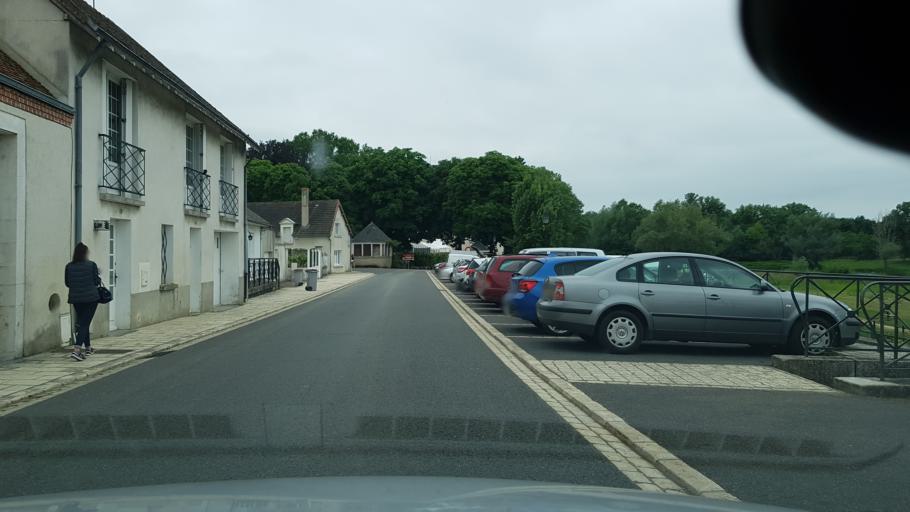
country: FR
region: Centre
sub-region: Departement du Loir-et-Cher
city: Selles-sur-Cher
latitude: 47.2761
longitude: 1.5511
